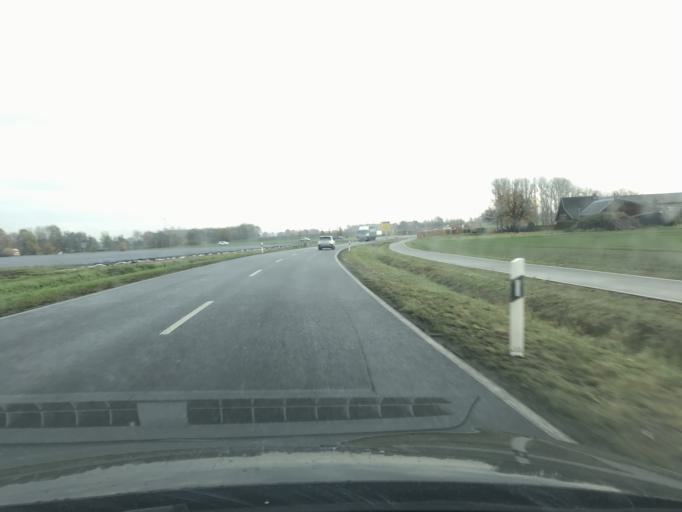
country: DE
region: North Rhine-Westphalia
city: Oelde
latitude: 51.8454
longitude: 8.1818
